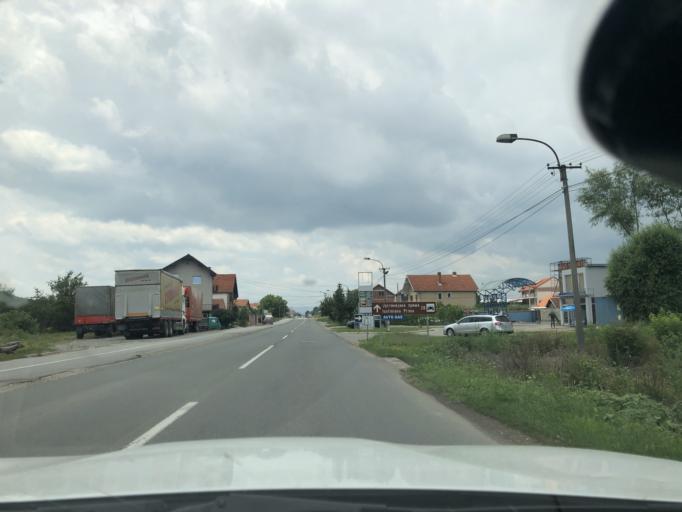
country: RS
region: Central Serbia
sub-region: Jablanicki Okrug
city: Leskovac
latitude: 42.9873
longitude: 21.9227
